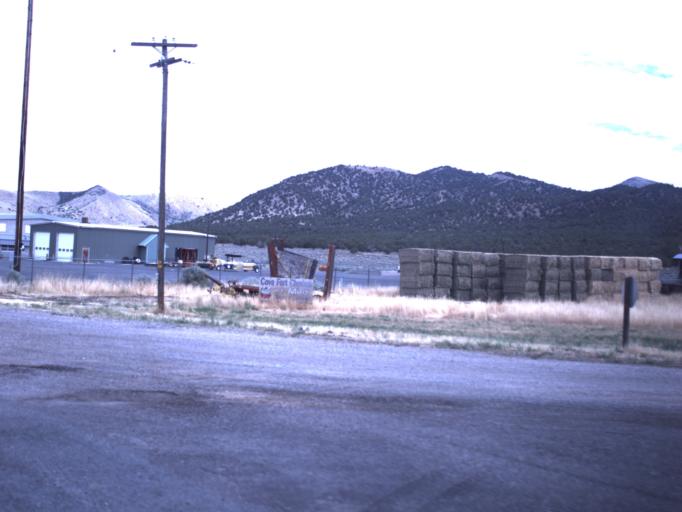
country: US
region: Utah
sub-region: Beaver County
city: Beaver
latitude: 38.6015
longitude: -112.5818
